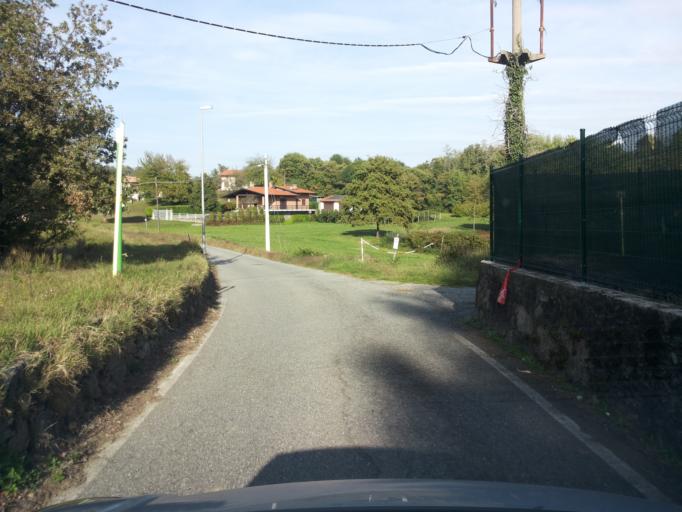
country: IT
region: Piedmont
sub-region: Provincia di Biella
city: Roppolo
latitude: 45.4267
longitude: 8.0735
